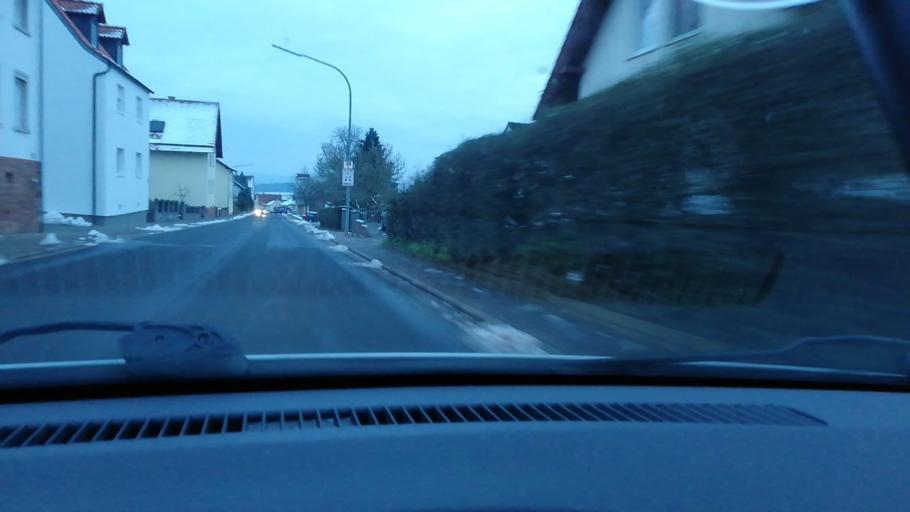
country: DE
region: Bavaria
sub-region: Regierungsbezirk Unterfranken
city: Geiselbach
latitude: 50.1253
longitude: 9.1911
